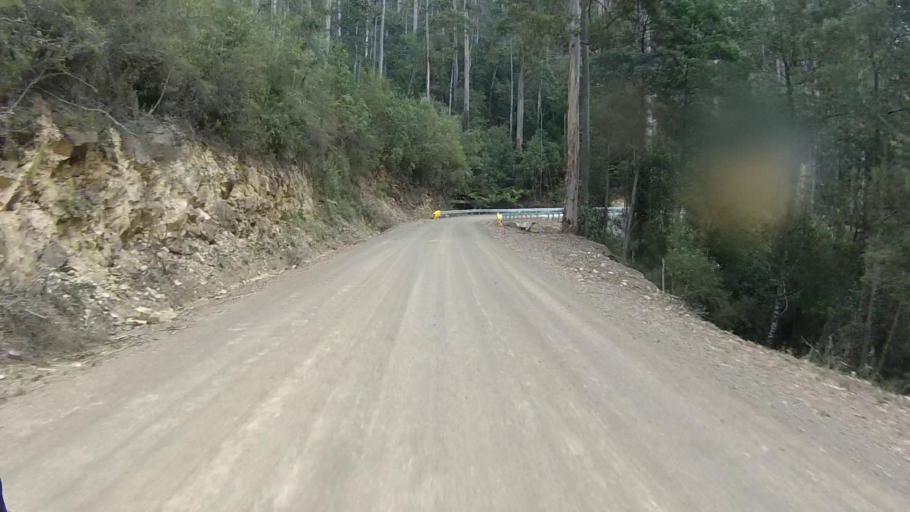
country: AU
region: Tasmania
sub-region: Sorell
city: Sorell
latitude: -42.6962
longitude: 147.8578
